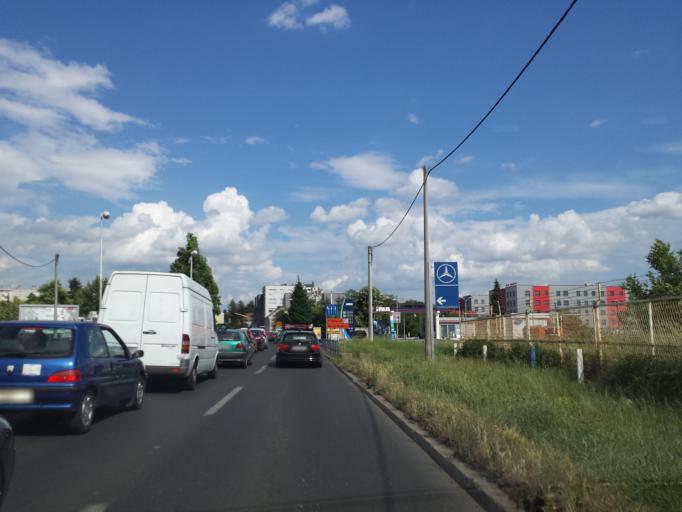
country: HR
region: Grad Zagreb
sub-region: Sesvete
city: Sesvete
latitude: 45.8278
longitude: 16.1044
